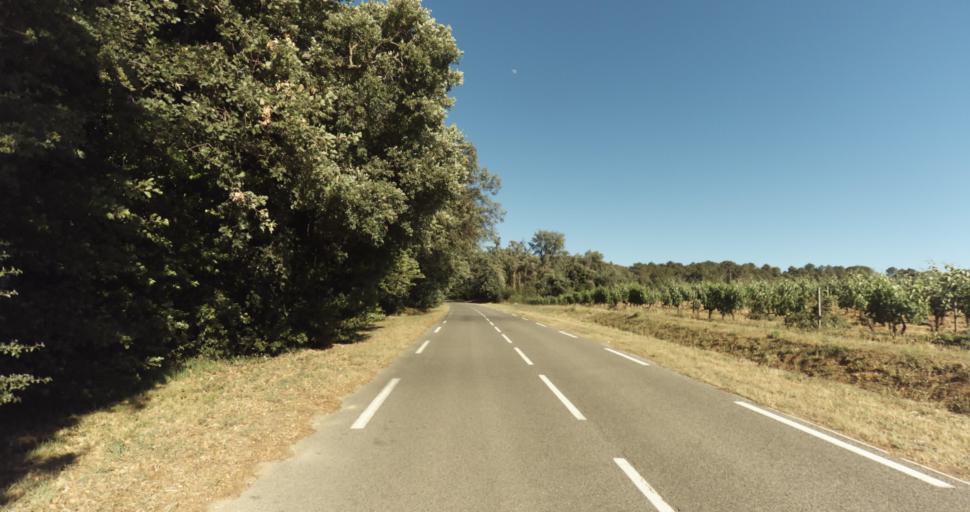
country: FR
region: Provence-Alpes-Cote d'Azur
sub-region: Departement du Var
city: Gassin
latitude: 43.2525
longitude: 6.5966
